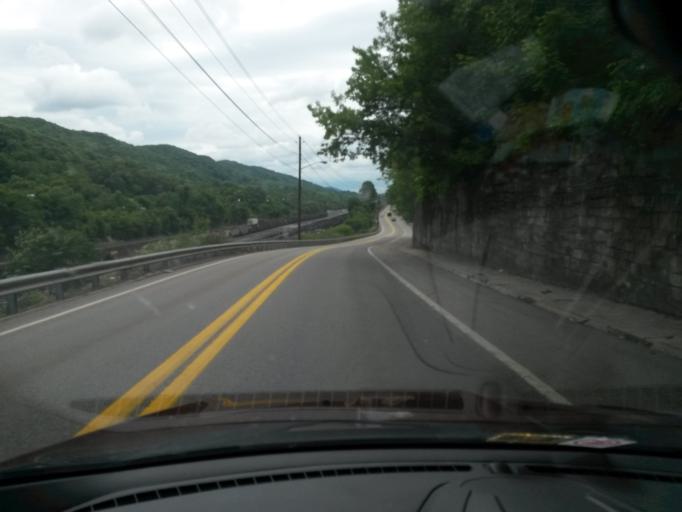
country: US
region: West Virginia
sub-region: Mercer County
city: Bluefield
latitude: 37.2744
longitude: -81.2097
